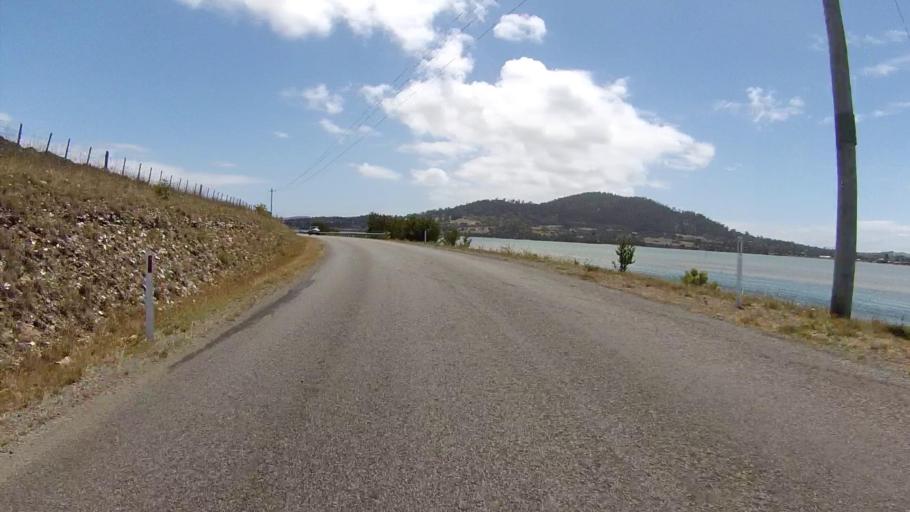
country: AU
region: Tasmania
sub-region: Clarence
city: Lauderdale
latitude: -42.9202
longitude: 147.4794
